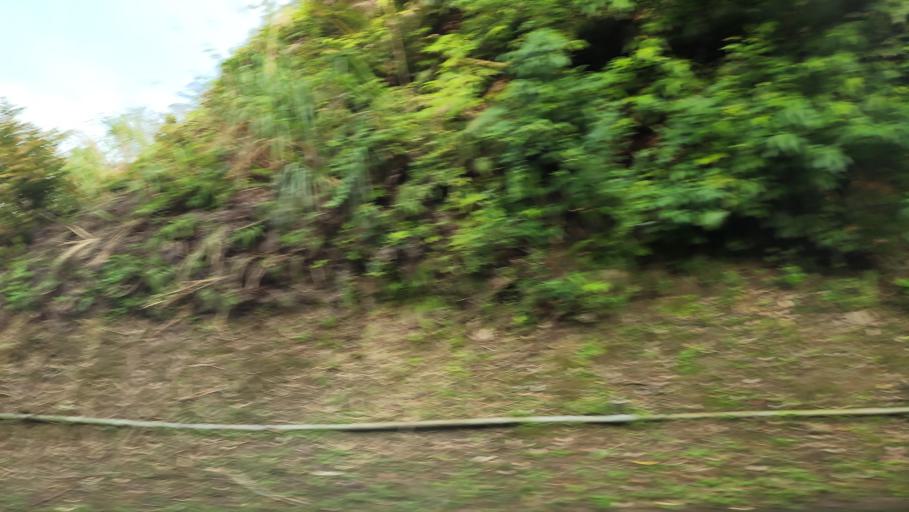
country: TW
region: Taiwan
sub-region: Keelung
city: Keelung
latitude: 25.1495
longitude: 121.6246
